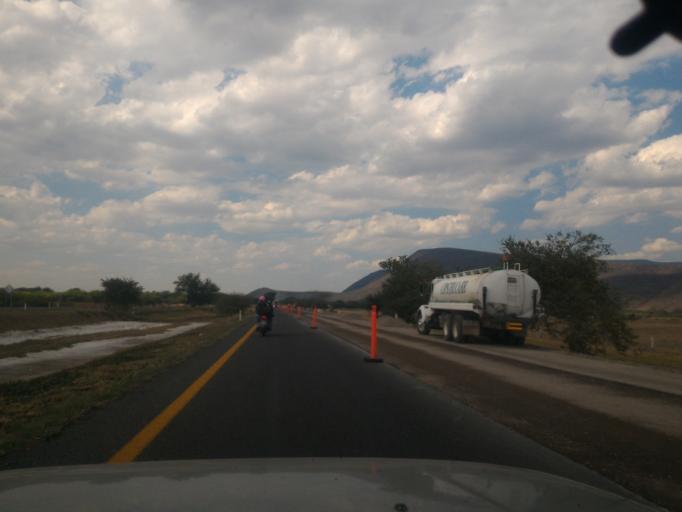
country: MX
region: Jalisco
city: Zacoalco de Torres
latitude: 20.1629
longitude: -103.5018
